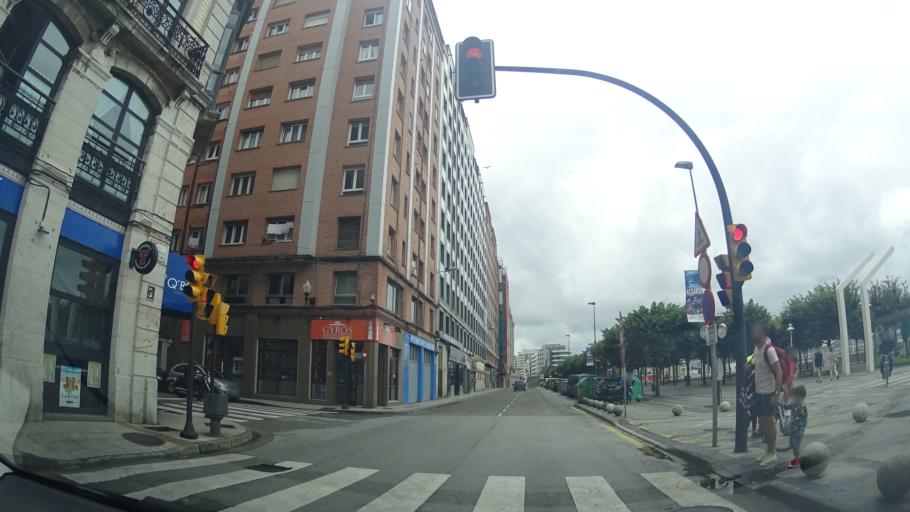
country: ES
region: Asturias
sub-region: Province of Asturias
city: Gijon
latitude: 43.5420
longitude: -5.6692
